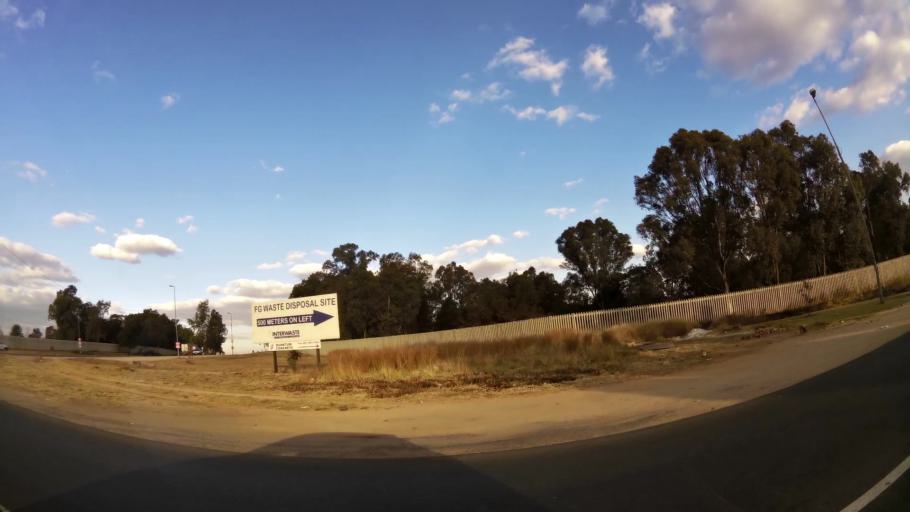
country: ZA
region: Gauteng
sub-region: Ekurhuleni Metropolitan Municipality
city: Tembisa
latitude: -25.9542
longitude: 28.1850
